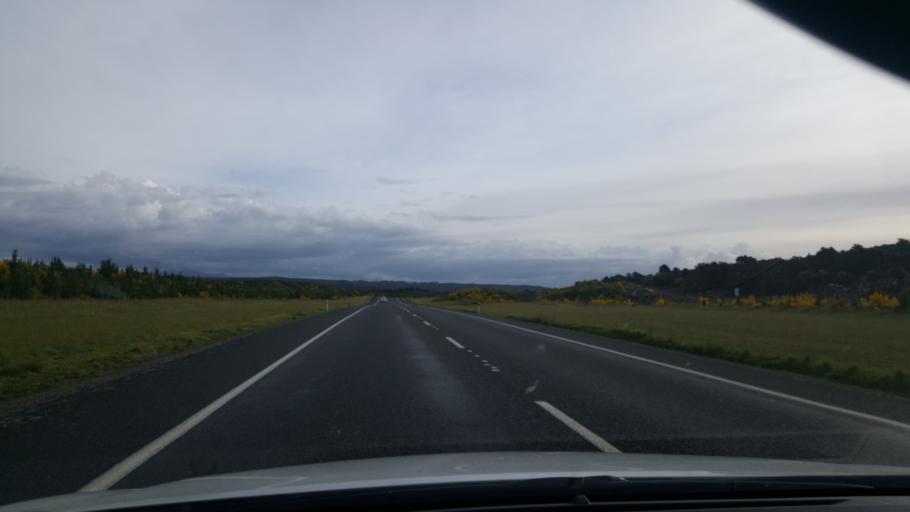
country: NZ
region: Waikato
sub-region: Taupo District
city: Taupo
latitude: -38.8474
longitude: 176.0573
